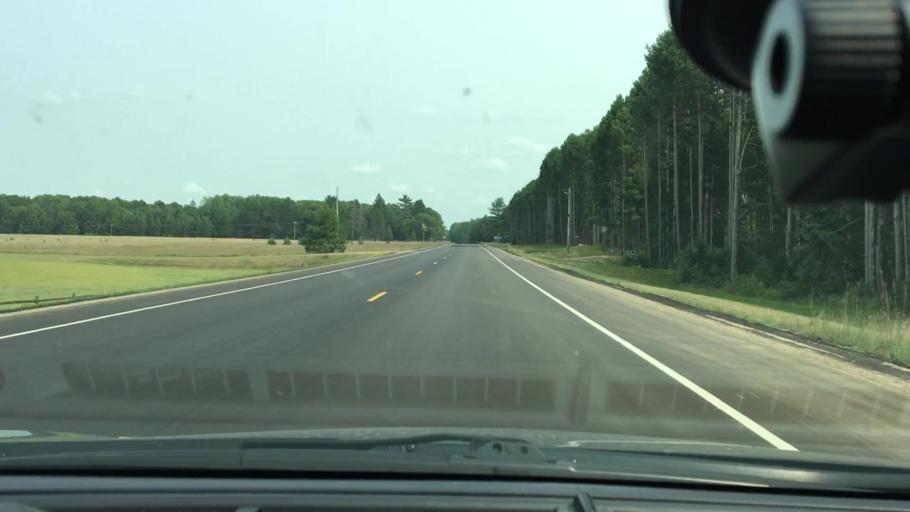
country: US
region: Minnesota
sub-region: Crow Wing County
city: Nisswa
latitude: 46.5293
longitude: -94.2516
